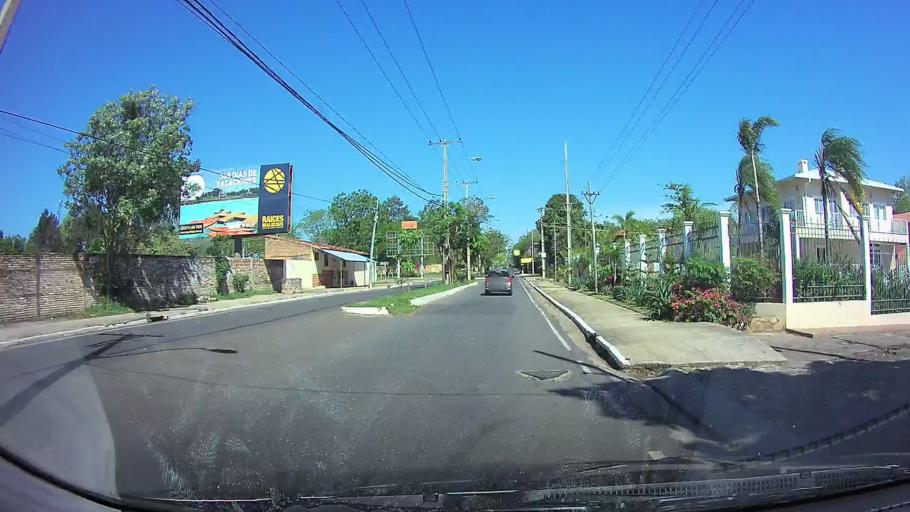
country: PY
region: Cordillera
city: San Bernardino
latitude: -25.2972
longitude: -57.3046
